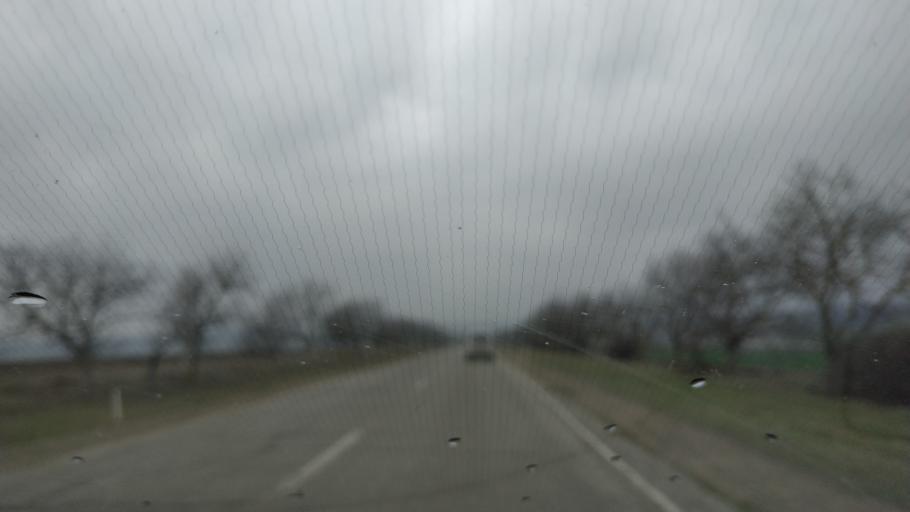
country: MD
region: Gagauzia
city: Comrat
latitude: 46.2512
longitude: 28.7577
